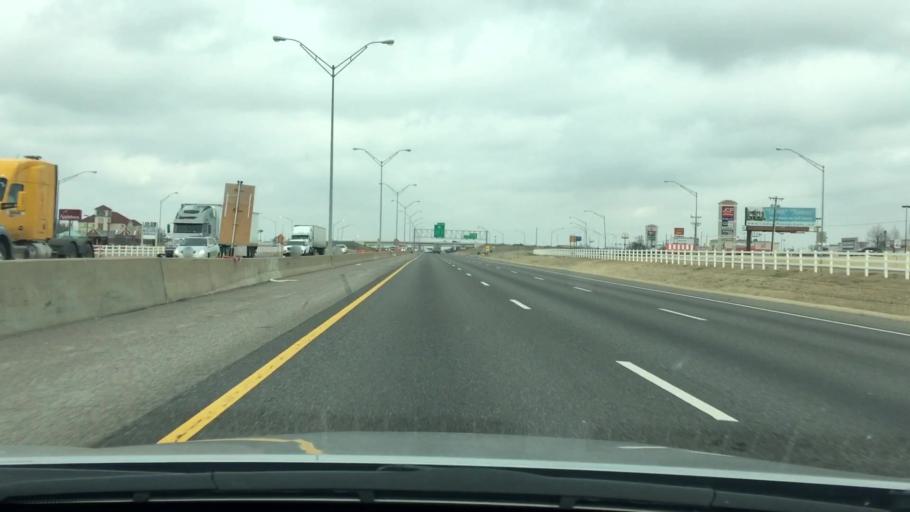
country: US
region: Oklahoma
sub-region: Cleveland County
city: Moore
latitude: 35.3140
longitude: -97.4900
